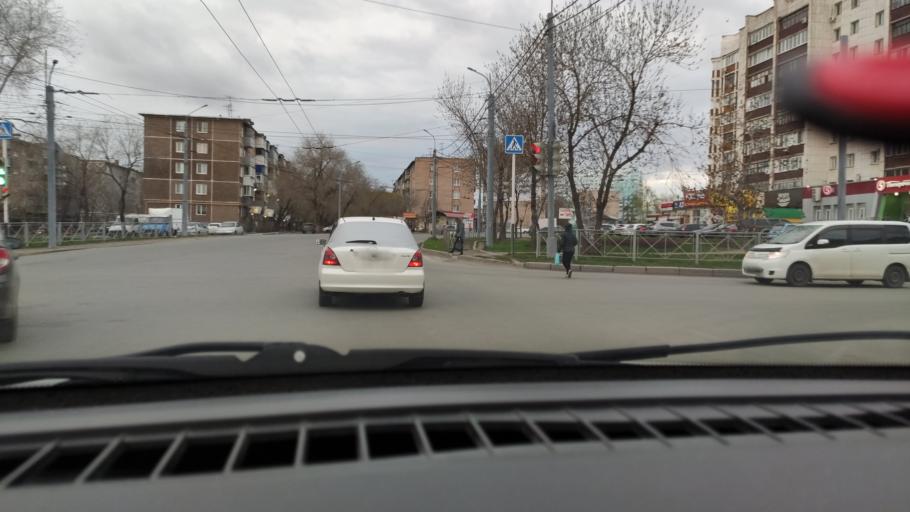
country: RU
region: Orenburg
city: Orenburg
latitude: 51.7850
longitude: 55.1531
